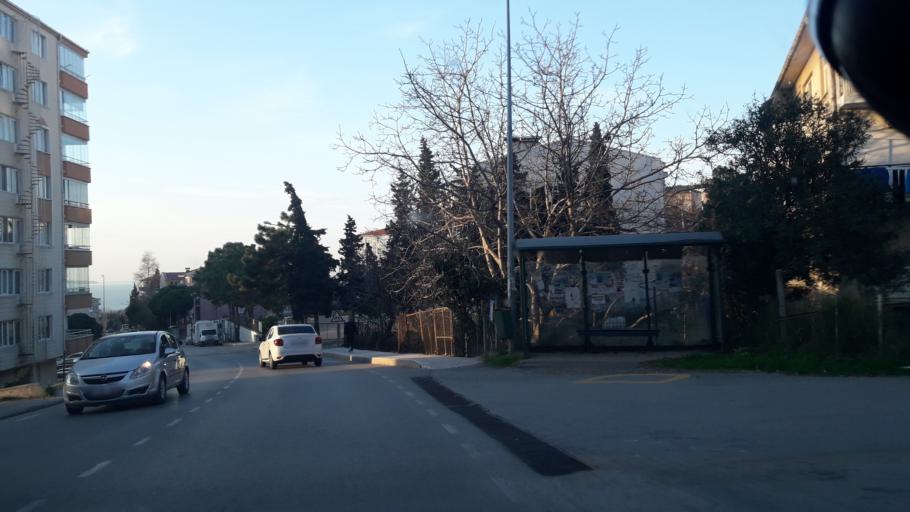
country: TR
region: Sinop
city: Sinop
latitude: 42.0272
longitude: 35.1606
